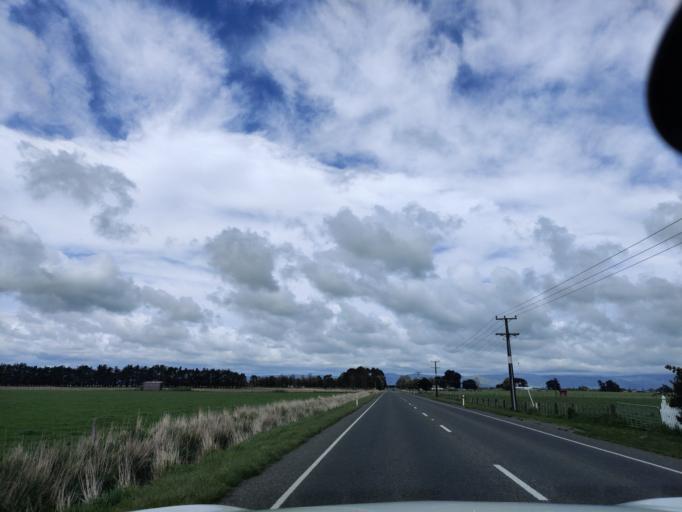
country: NZ
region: Manawatu-Wanganui
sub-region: Palmerston North City
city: Palmerston North
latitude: -40.3222
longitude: 175.5014
